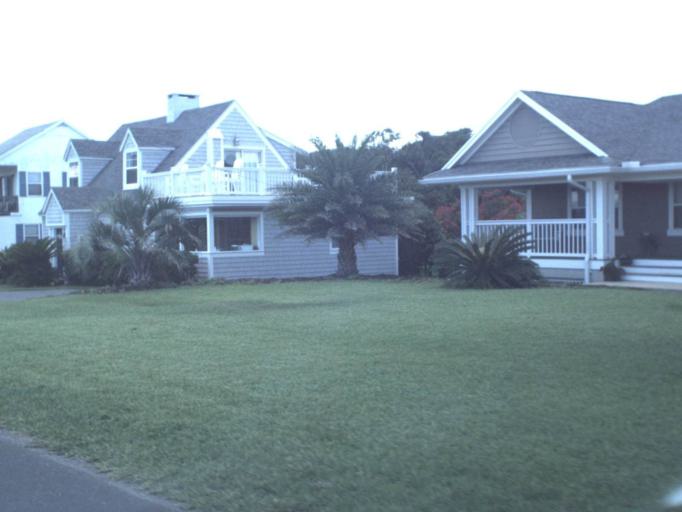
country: US
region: Florida
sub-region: Nassau County
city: Fernandina Beach
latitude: 30.6098
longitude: -81.4426
